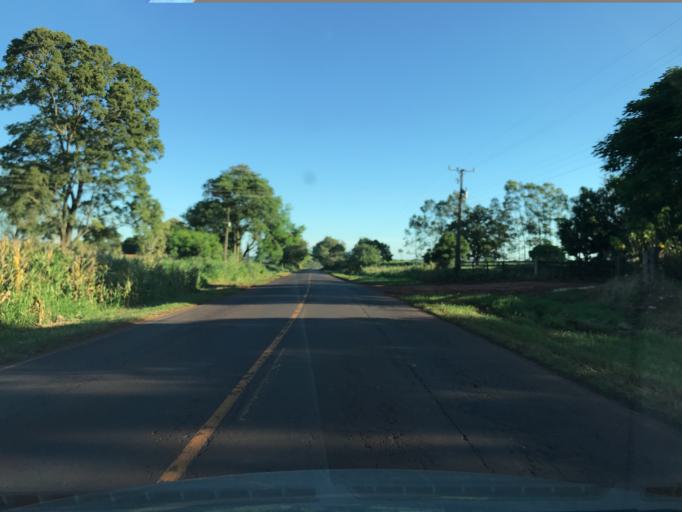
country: BR
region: Parana
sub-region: Ipora
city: Ipora
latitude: -24.0890
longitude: -53.8351
